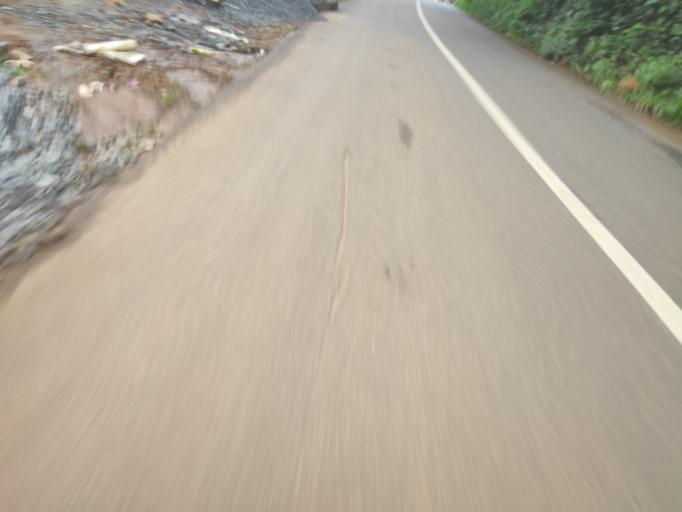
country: IN
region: Kerala
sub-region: Malappuram
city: Manjeri
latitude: 11.1666
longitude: 76.1744
